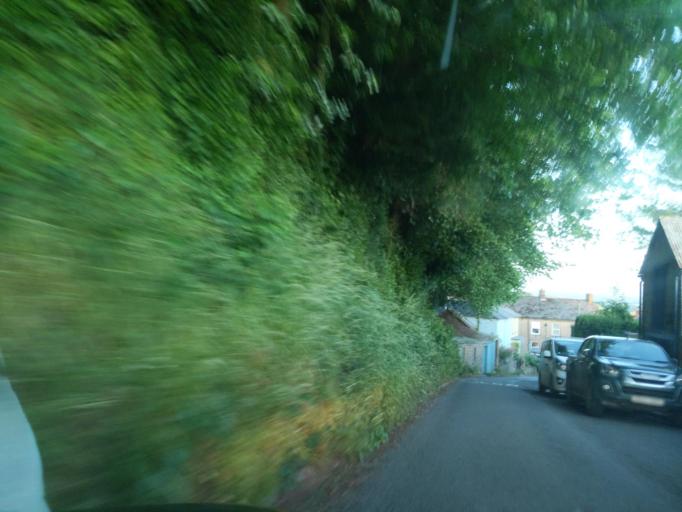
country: GB
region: England
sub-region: Devon
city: Okehampton
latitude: 50.8232
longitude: -4.0712
